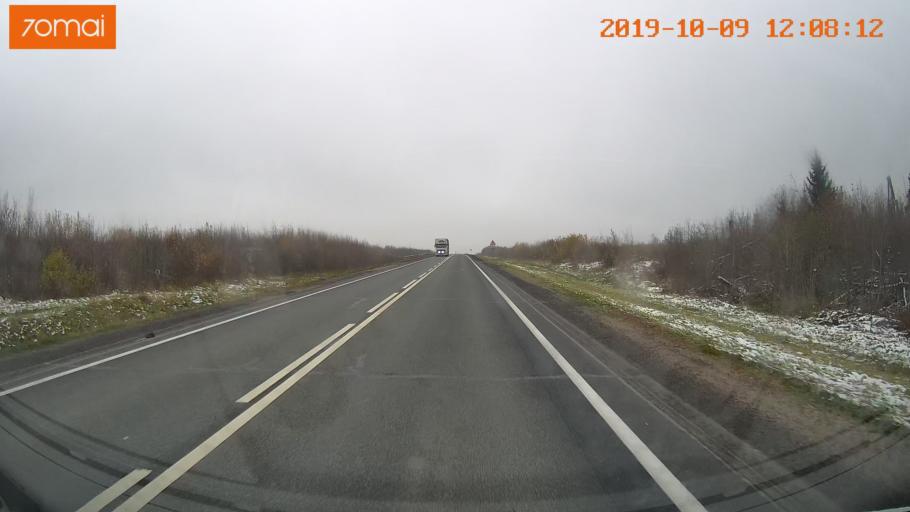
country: RU
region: Jaroslavl
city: Prechistoye
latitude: 58.5897
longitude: 40.3465
